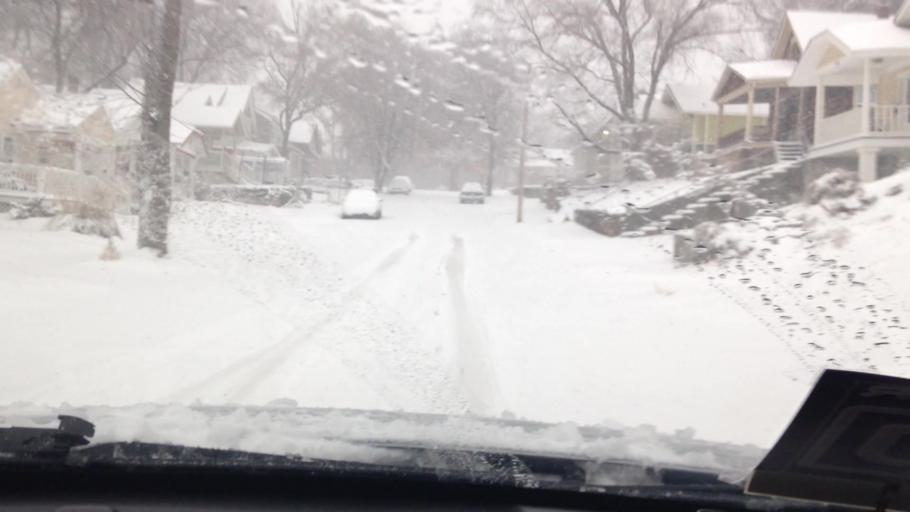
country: US
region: Kansas
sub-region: Johnson County
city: Westwood
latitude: 39.0417
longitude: -94.6035
